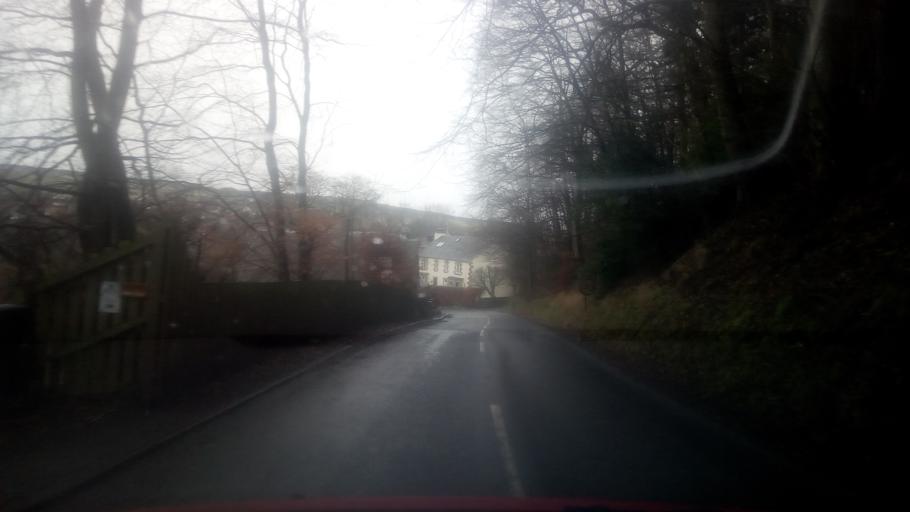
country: GB
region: Scotland
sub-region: The Scottish Borders
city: Earlston
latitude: 55.6343
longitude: -2.6756
